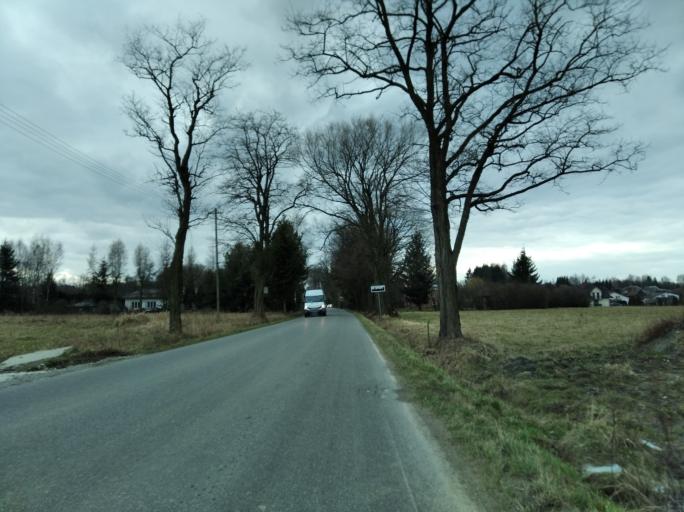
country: PL
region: Subcarpathian Voivodeship
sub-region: Powiat krosnienski
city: Odrzykon
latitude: 49.7494
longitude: 21.7054
